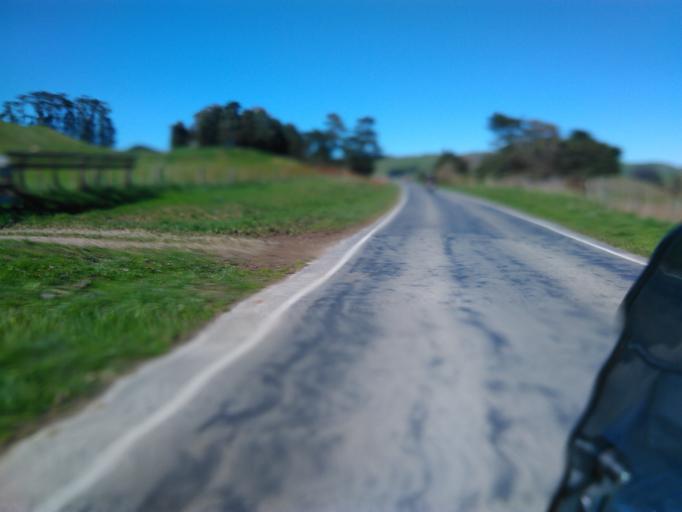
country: NZ
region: Bay of Plenty
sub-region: Opotiki District
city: Opotiki
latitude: -38.3457
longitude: 177.5327
